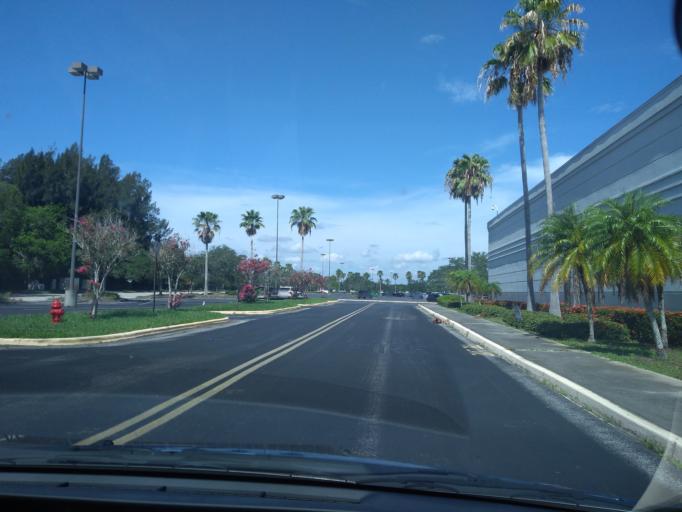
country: US
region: Florida
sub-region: Indian River County
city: West Vero Corridor
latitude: 27.6411
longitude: -80.4577
